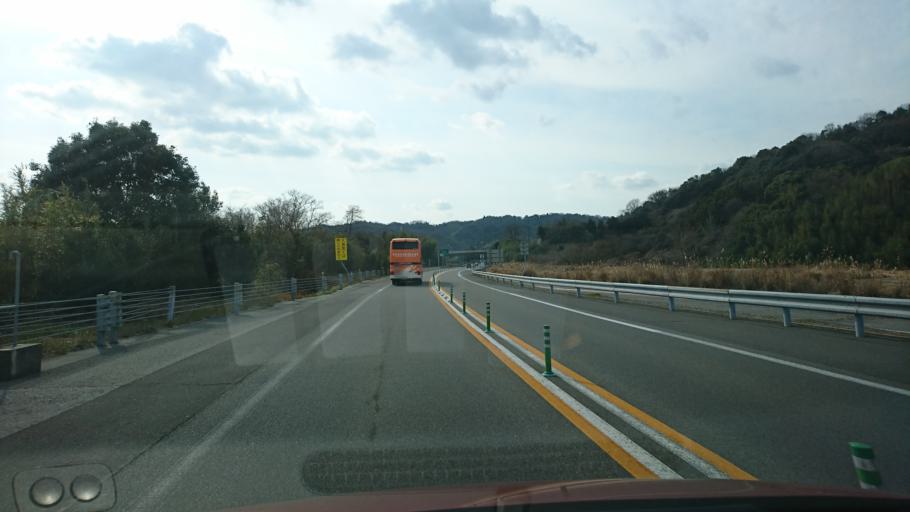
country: JP
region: Hiroshima
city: Innoshima
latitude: 34.1734
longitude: 133.0673
